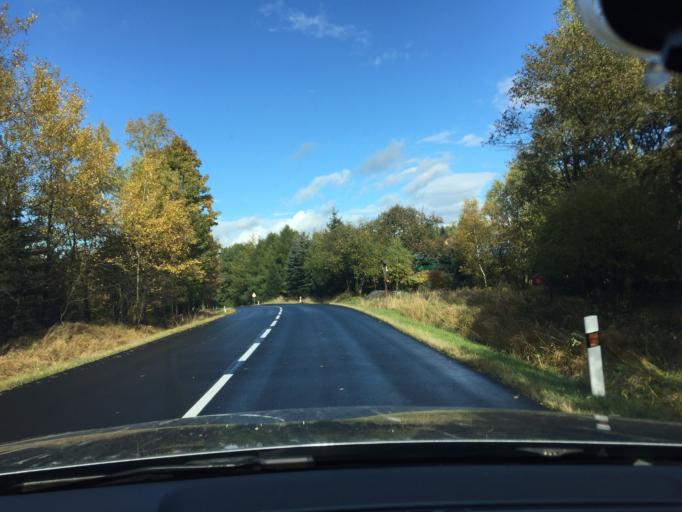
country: CZ
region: Ustecky
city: Libouchec
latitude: 50.7588
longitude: 13.9751
